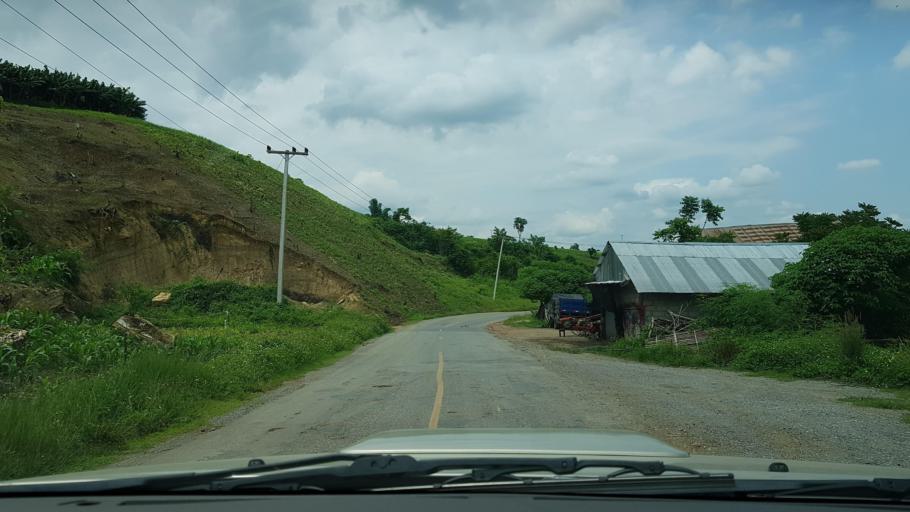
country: TH
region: Nan
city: Chaloem Phra Kiat
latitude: 20.0202
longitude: 101.3239
